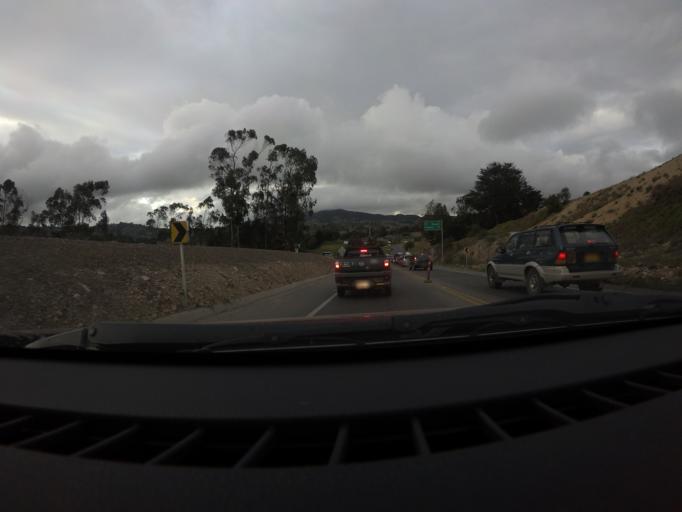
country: CO
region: Boyaca
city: Samaca
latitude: 5.4539
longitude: -73.4253
